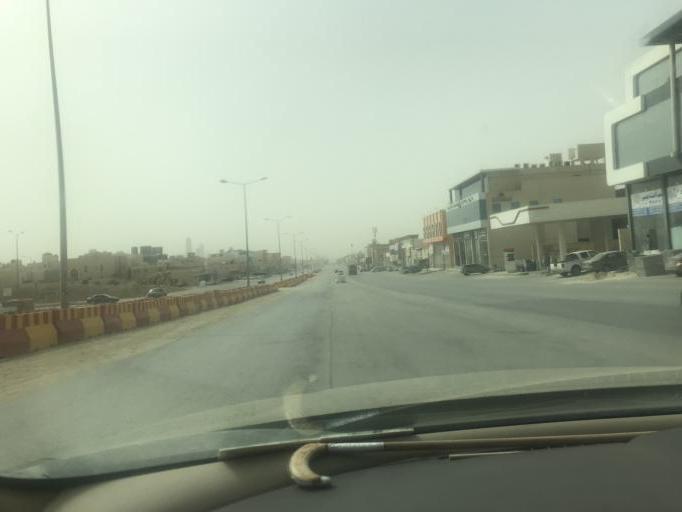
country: SA
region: Ar Riyad
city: Riyadh
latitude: 24.8109
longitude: 46.6002
